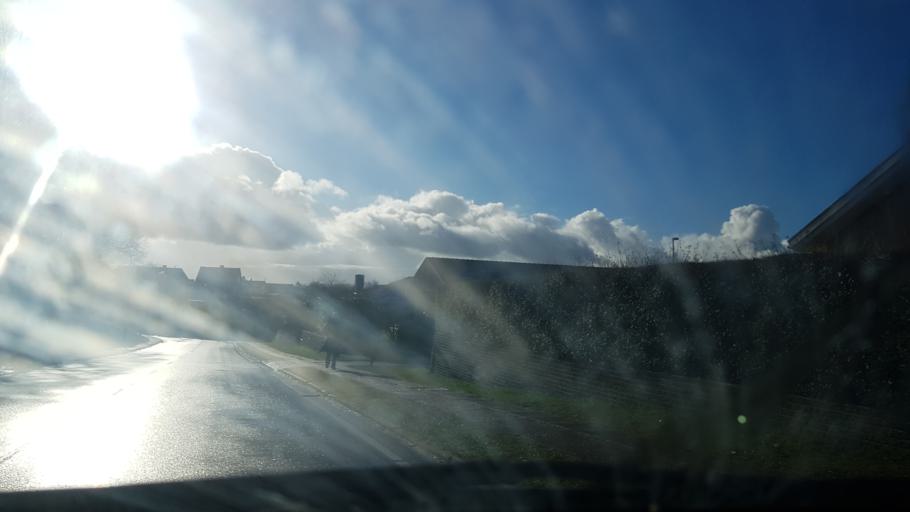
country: DK
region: South Denmark
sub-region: Fredericia Kommune
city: Taulov
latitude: 55.5158
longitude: 9.6379
